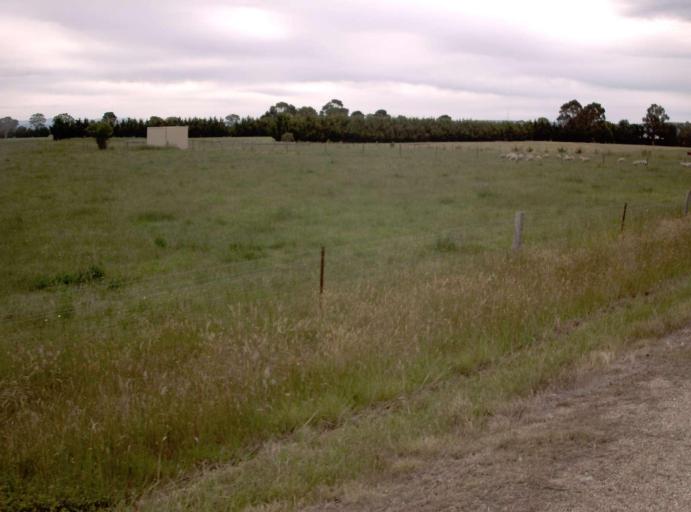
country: AU
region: Victoria
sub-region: East Gippsland
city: Bairnsdale
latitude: -37.8689
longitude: 147.5616
